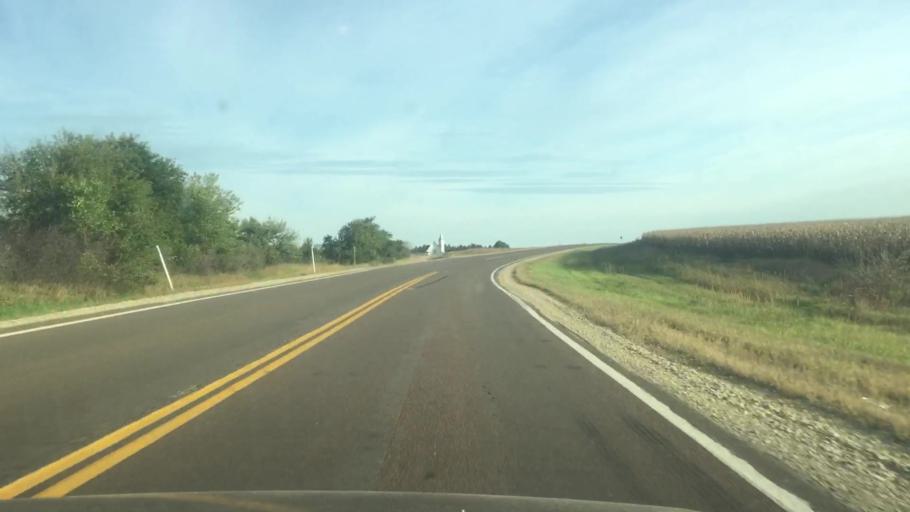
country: US
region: Nebraska
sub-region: Gage County
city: Wymore
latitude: 39.9961
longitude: -96.6574
